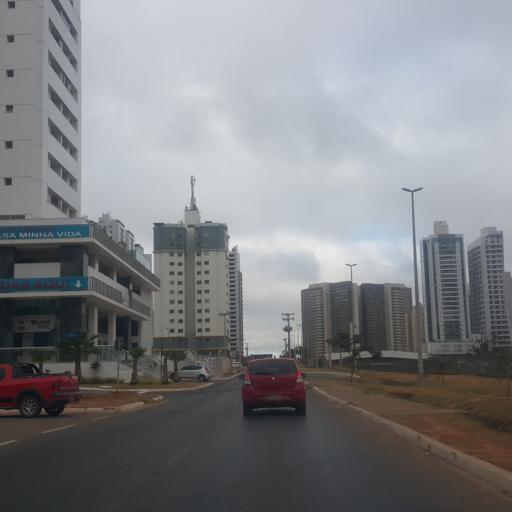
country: BR
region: Federal District
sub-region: Brasilia
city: Brasilia
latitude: -15.8374
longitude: -48.0363
